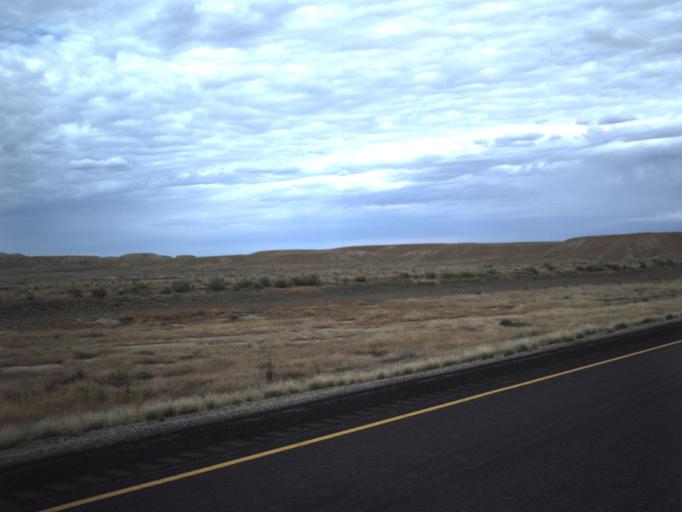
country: US
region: Utah
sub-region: Grand County
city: Moab
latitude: 38.9435
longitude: -109.6410
